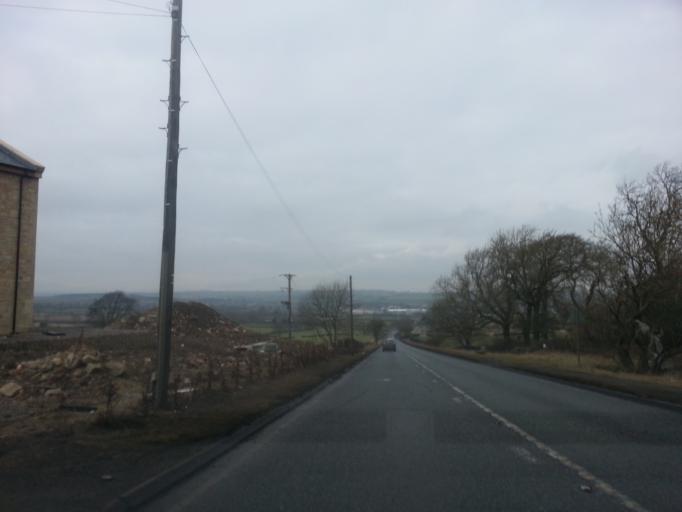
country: GB
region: England
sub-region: County Durham
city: Bishop Auckland
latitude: 54.6178
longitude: -1.7030
